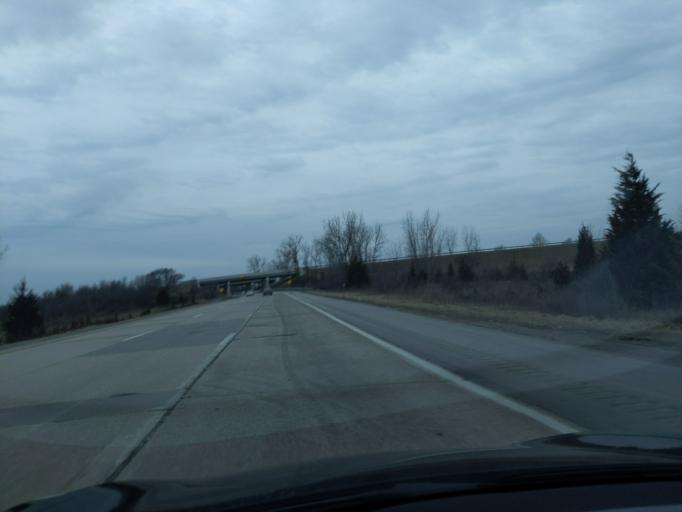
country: US
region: Michigan
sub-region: Bay County
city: Bay City
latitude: 43.6209
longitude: -83.9471
